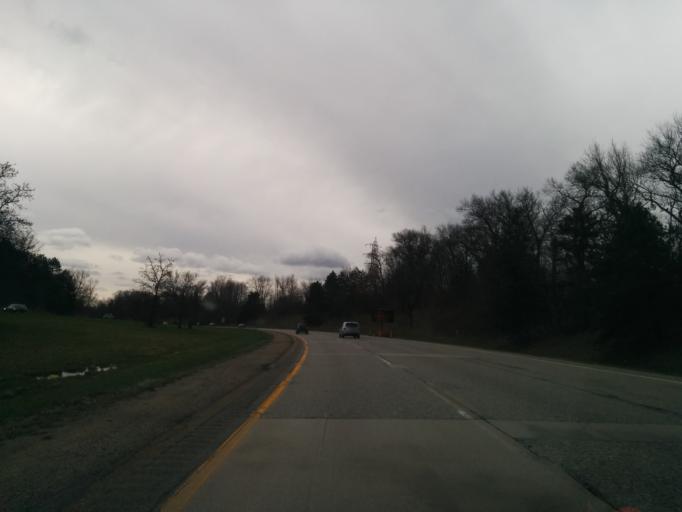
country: US
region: Michigan
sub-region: Kent County
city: Grand Rapids
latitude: 42.9629
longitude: -85.7087
